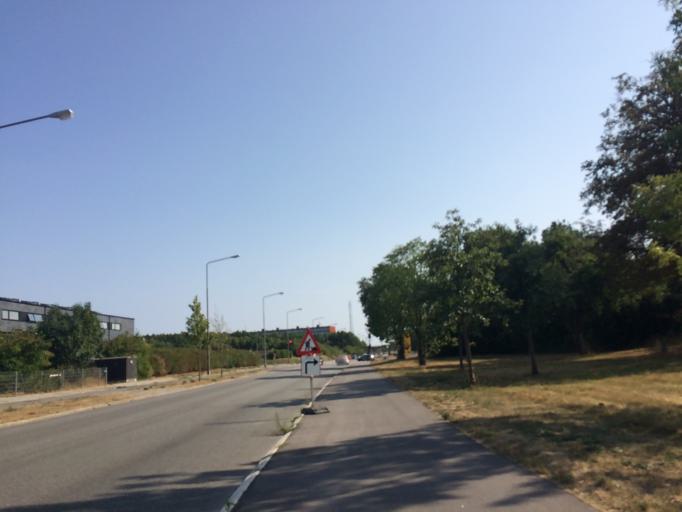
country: DK
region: Capital Region
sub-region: Hvidovre Kommune
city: Hvidovre
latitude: 55.6290
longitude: 12.4560
